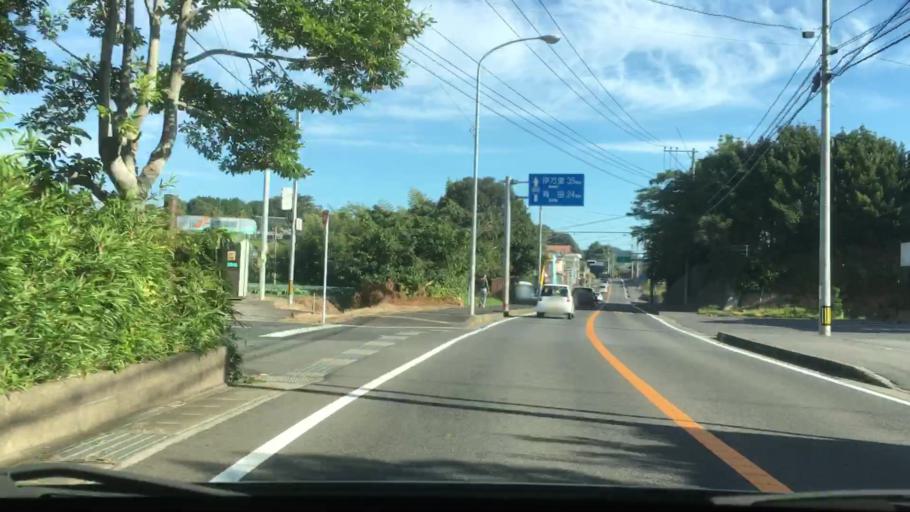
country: JP
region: Nagasaki
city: Sasebo
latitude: 33.0603
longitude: 129.7630
